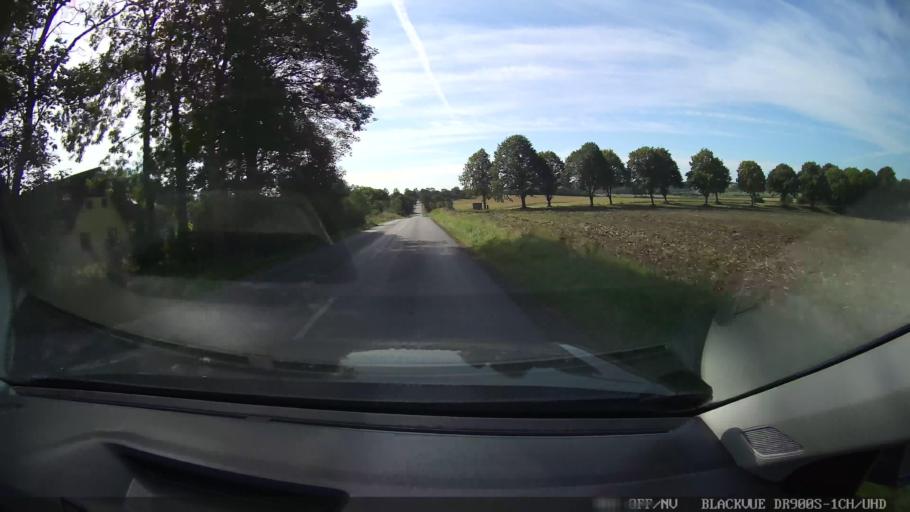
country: DK
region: North Denmark
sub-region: Mariagerfjord Kommune
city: Hobro
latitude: 56.5569
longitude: 9.8434
